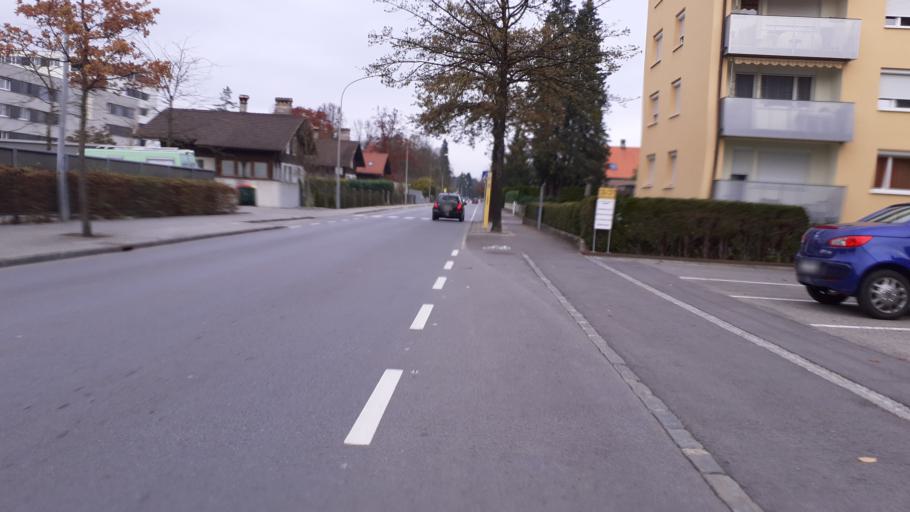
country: AT
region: Vorarlberg
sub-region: Politischer Bezirk Feldkirch
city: Nofels
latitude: 47.2447
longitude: 9.5895
